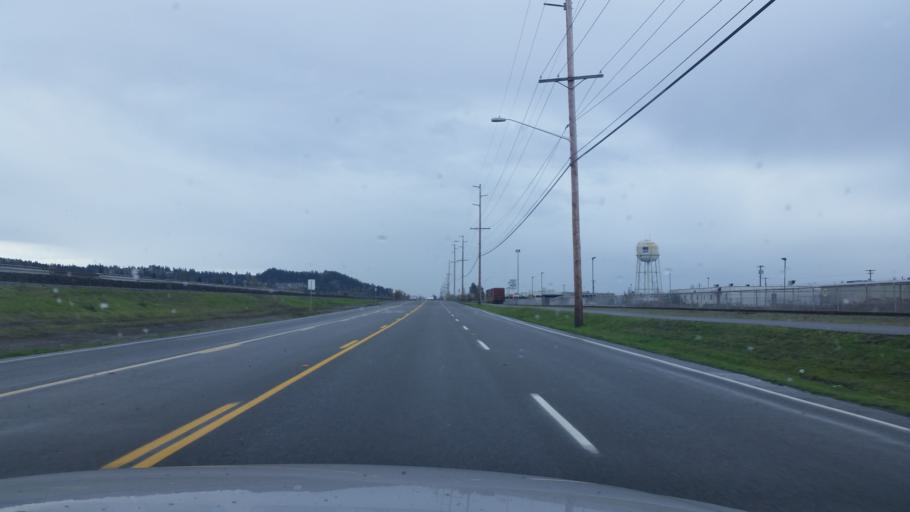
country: US
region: Washington
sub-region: King County
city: Auburn
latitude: 47.2883
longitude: -122.2317
